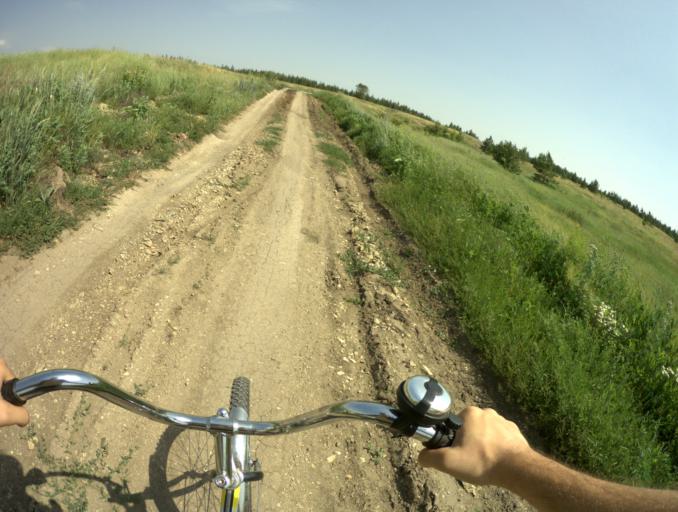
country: RU
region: Saratov
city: Yelshanka
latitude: 51.8331
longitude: 46.4875
